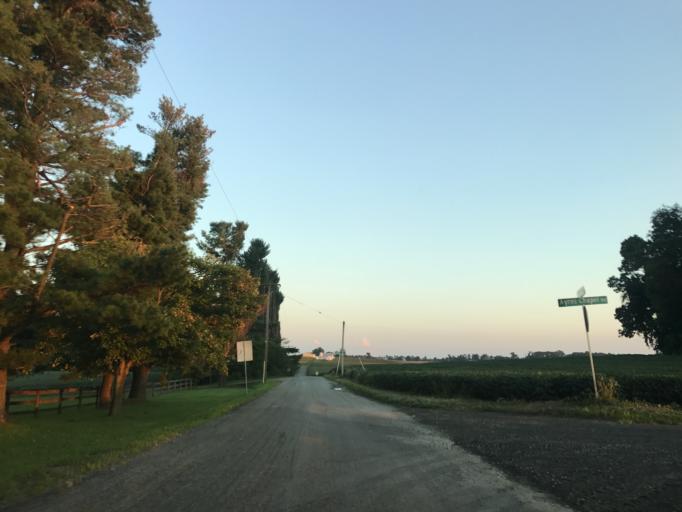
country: US
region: Maryland
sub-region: Harford County
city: Jarrettsville
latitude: 39.6652
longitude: -76.5292
